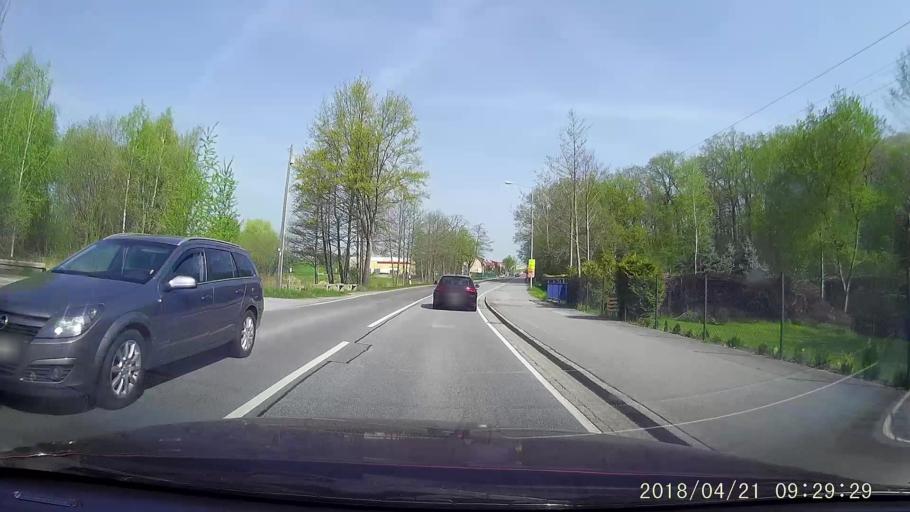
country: DE
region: Saxony
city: Bautzen
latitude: 51.1927
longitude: 14.4101
